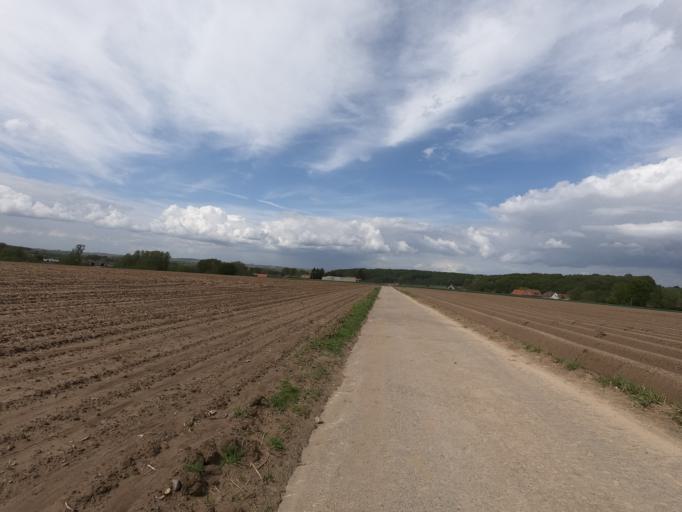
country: BE
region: Flanders
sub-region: Provincie Oost-Vlaanderen
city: Ronse
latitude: 50.7761
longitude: 3.5786
